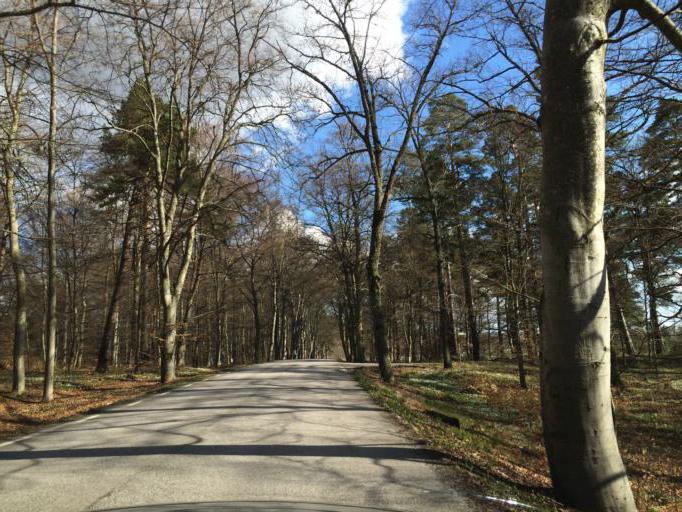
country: SE
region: Soedermanland
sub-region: Eskilstuna Kommun
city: Eskilstuna
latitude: 59.4426
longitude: 16.6253
